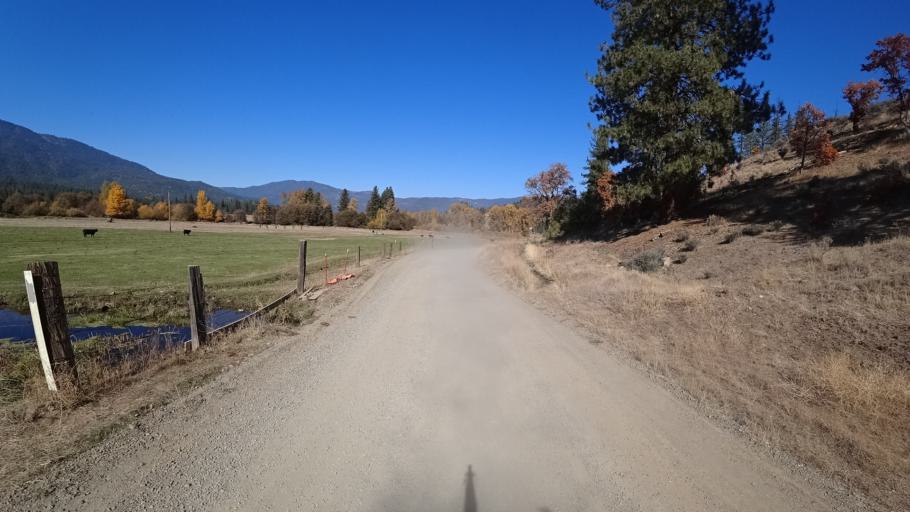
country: US
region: California
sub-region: Siskiyou County
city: Yreka
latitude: 41.5982
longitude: -122.9582
